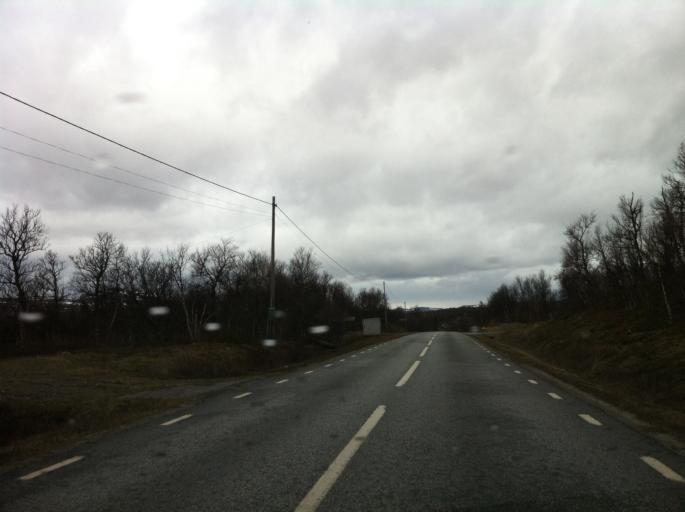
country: NO
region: Sor-Trondelag
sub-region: Tydal
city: Aas
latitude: 62.6052
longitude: 12.1660
